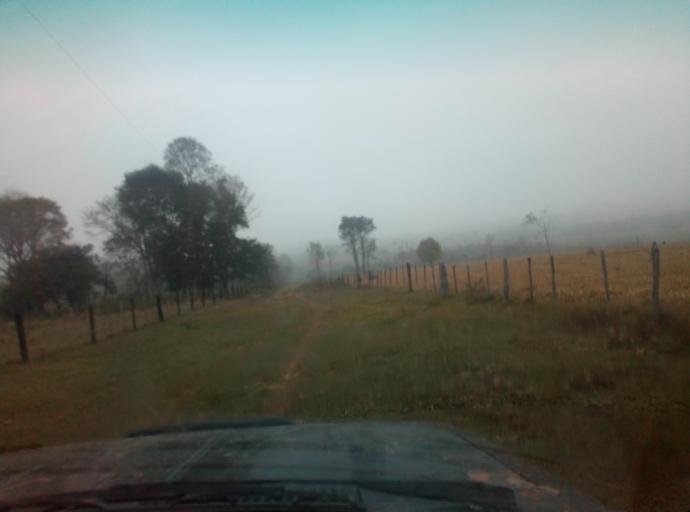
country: PY
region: Caaguazu
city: Doctor Cecilio Baez
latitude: -25.1503
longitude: -56.2605
